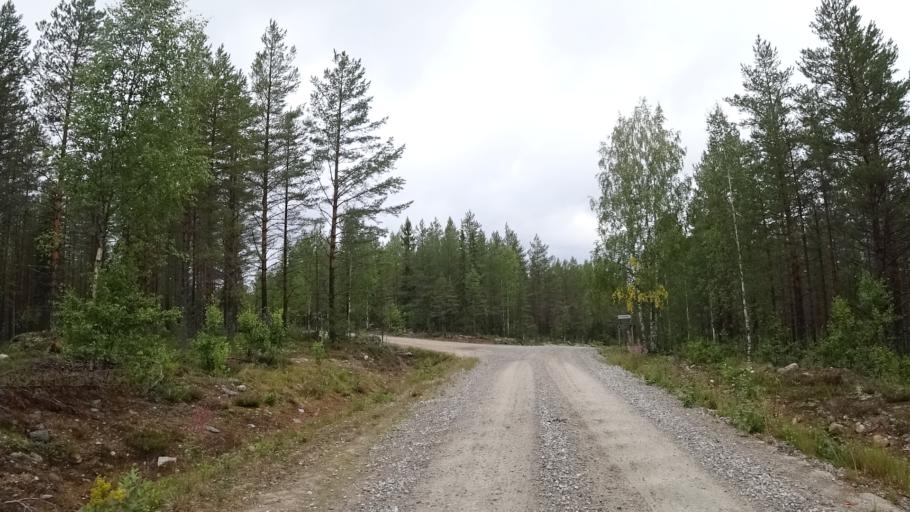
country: FI
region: North Karelia
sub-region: Pielisen Karjala
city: Lieksa
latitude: 63.4774
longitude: 30.2587
